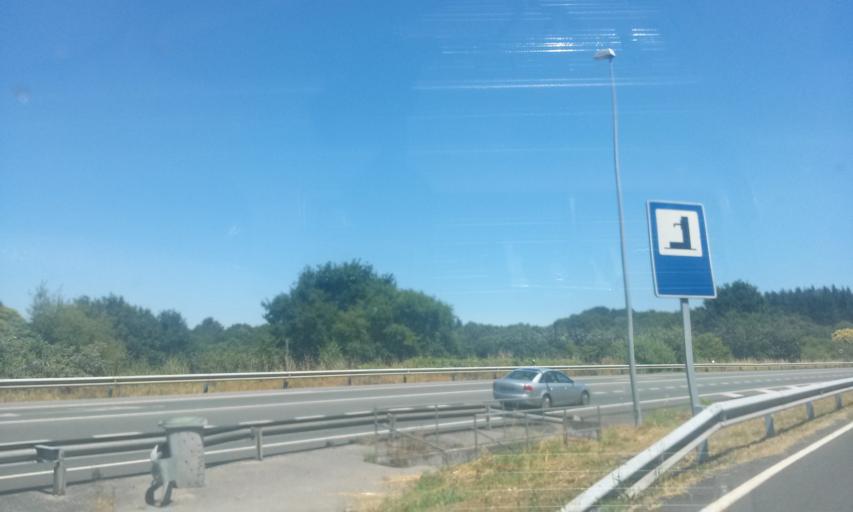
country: ES
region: Galicia
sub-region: Provincia de Lugo
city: Lugo
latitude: 43.0254
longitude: -7.5775
